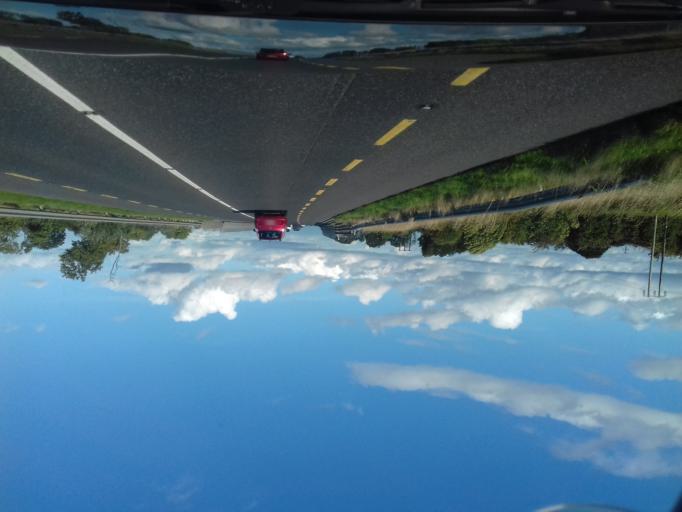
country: IE
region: Leinster
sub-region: Uibh Fhaili
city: Tullamore
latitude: 53.2600
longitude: -7.4664
